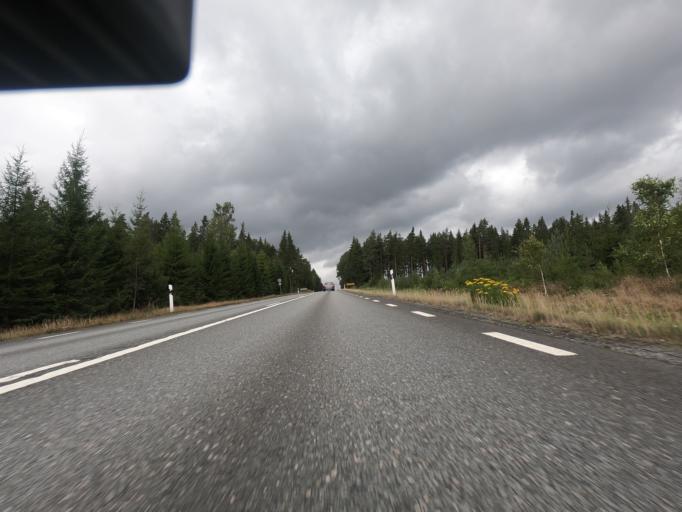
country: SE
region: Joenkoeping
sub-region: Savsjo Kommun
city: Vrigstad
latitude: 57.4079
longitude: 14.3525
